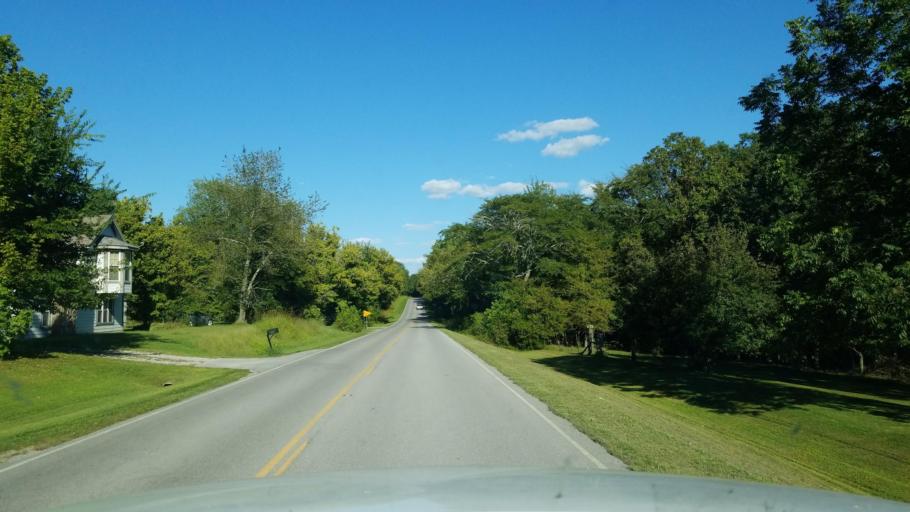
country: US
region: Illinois
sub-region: Hardin County
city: Elizabethtown
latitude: 37.5772
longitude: -88.3827
